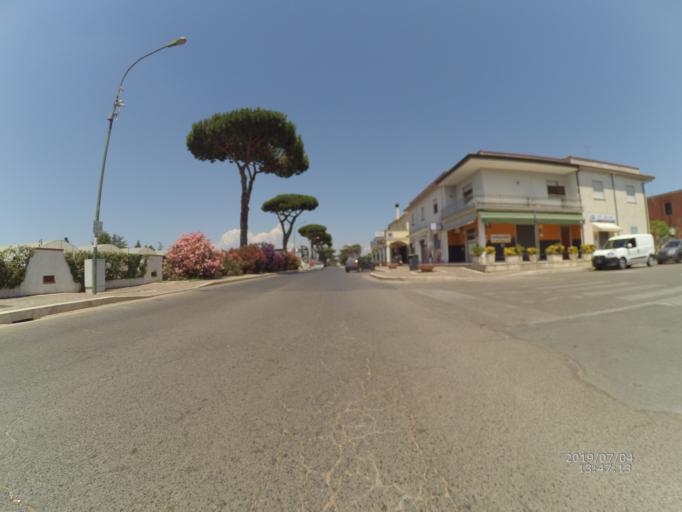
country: IT
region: Latium
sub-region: Provincia di Latina
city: San Felice Circeo
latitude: 41.2767
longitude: 13.1009
